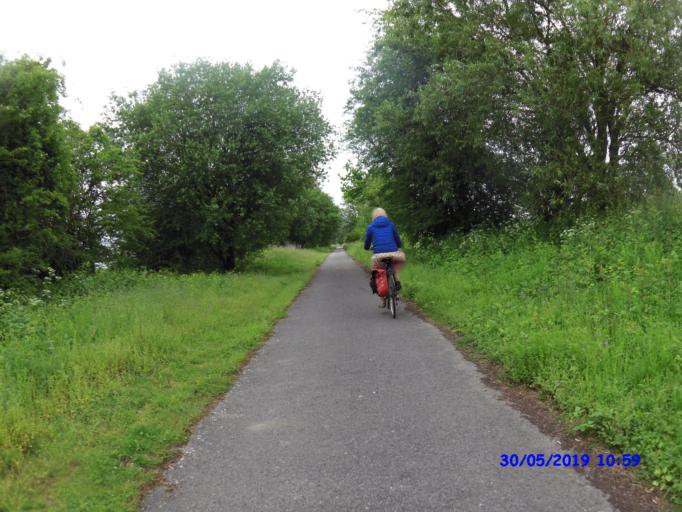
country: BE
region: Wallonia
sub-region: Province du Hainaut
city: Thuin
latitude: 50.2728
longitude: 4.3060
